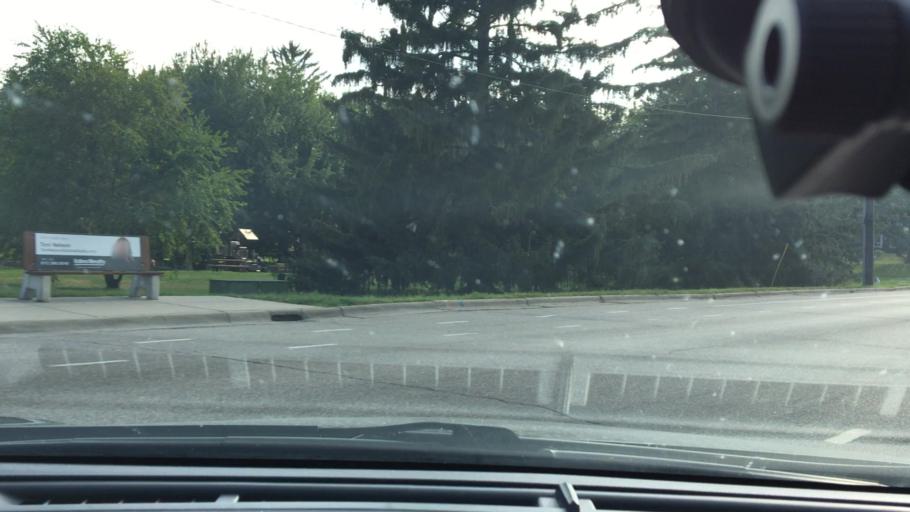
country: US
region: Minnesota
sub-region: Hennepin County
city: Richfield
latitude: 44.9053
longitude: -93.2527
